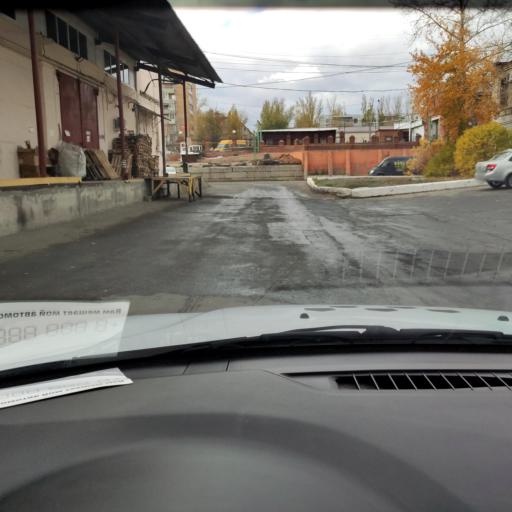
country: RU
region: Samara
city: Zhigulevsk
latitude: 53.4835
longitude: 49.4882
